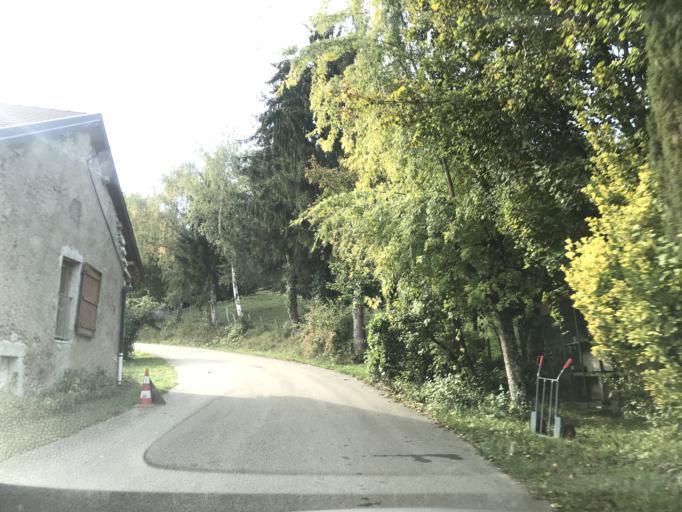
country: FR
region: Rhone-Alpes
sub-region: Departement de la Savoie
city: Yenne
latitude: 45.6901
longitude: 5.7959
